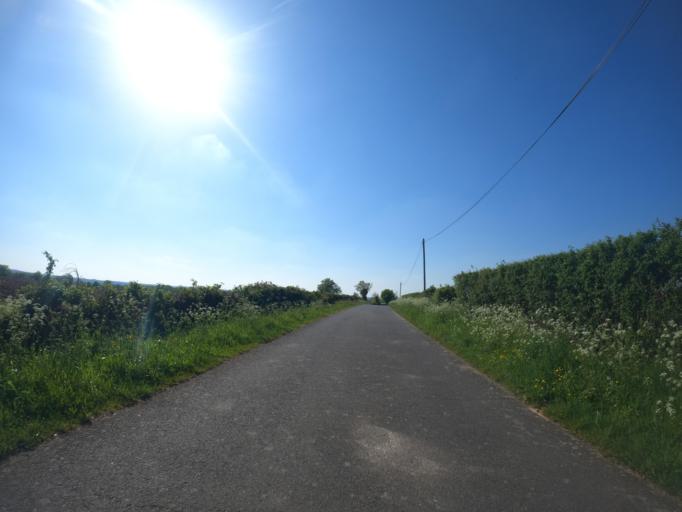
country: FR
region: Poitou-Charentes
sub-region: Departement des Deux-Sevres
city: Moncoutant
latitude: 46.6833
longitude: -0.5291
